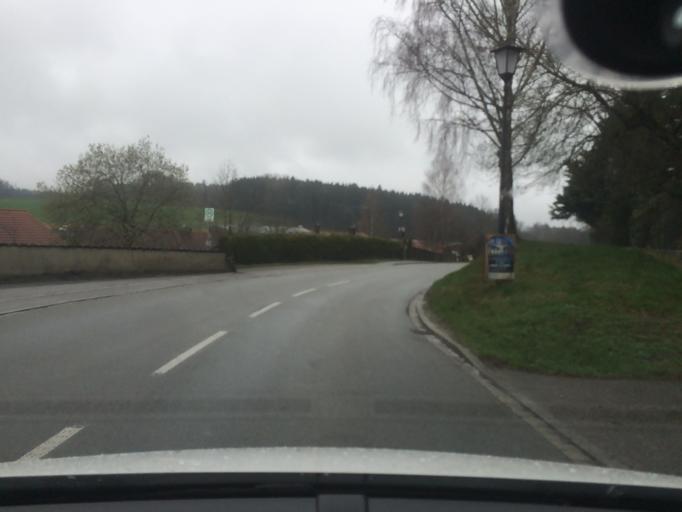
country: DE
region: Bavaria
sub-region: Upper Bavaria
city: Assling
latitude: 47.9773
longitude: 11.9563
